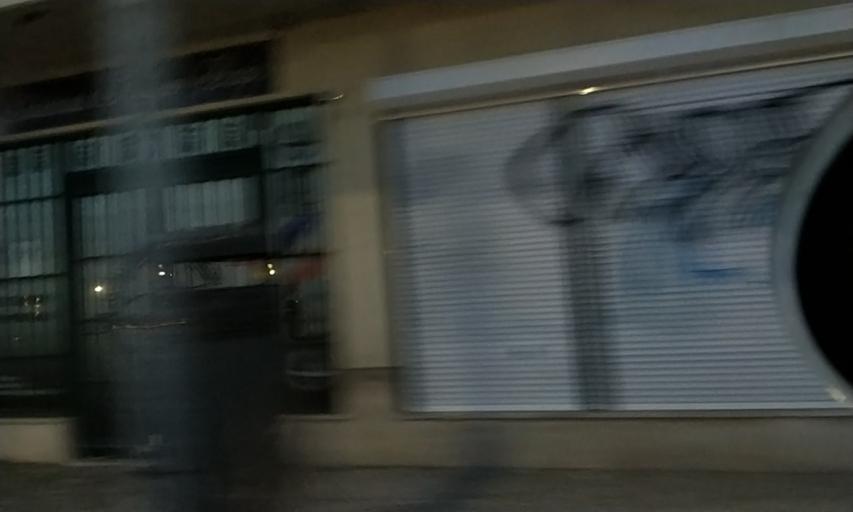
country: PT
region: Setubal
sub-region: Setubal
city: Setubal
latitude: 38.5291
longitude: -8.8902
